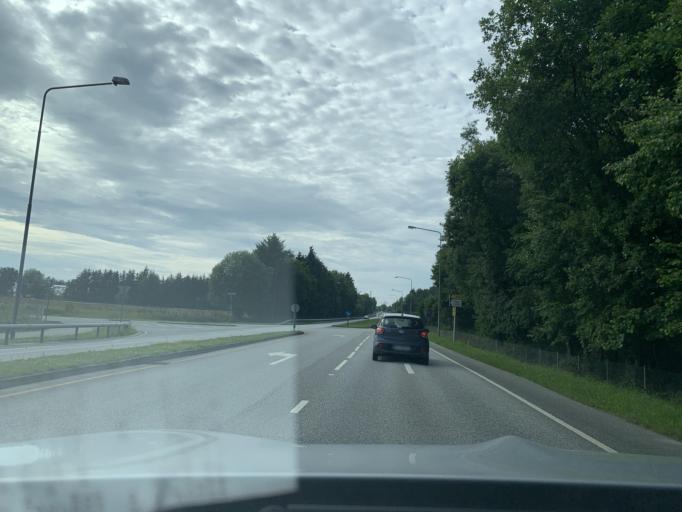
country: NO
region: Rogaland
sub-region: Stavanger
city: Stavanger
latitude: 58.9169
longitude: 5.7187
